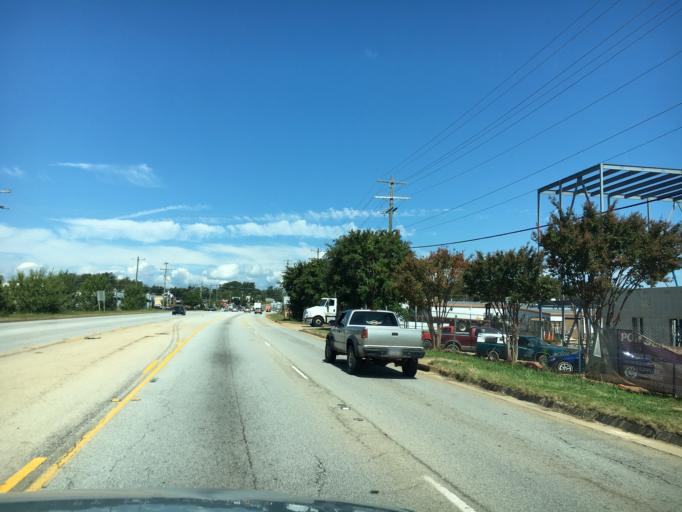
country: US
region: South Carolina
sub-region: Greenville County
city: Greer
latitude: 34.9395
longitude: -82.2570
